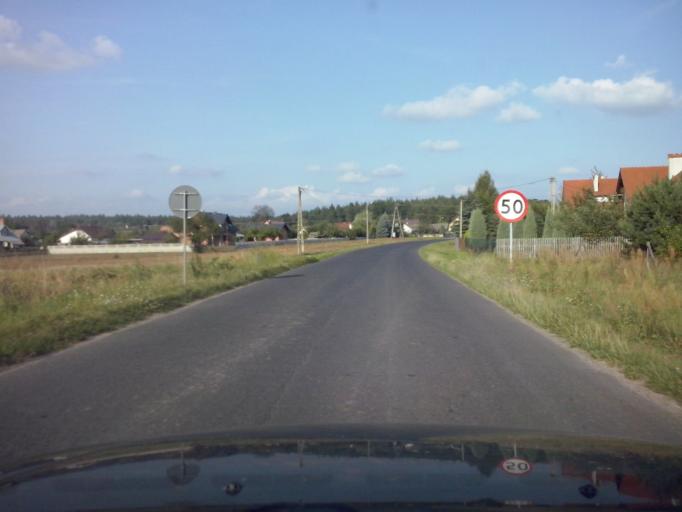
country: PL
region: Subcarpathian Voivodeship
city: Nowa Sarzyna
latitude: 50.3066
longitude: 22.2997
